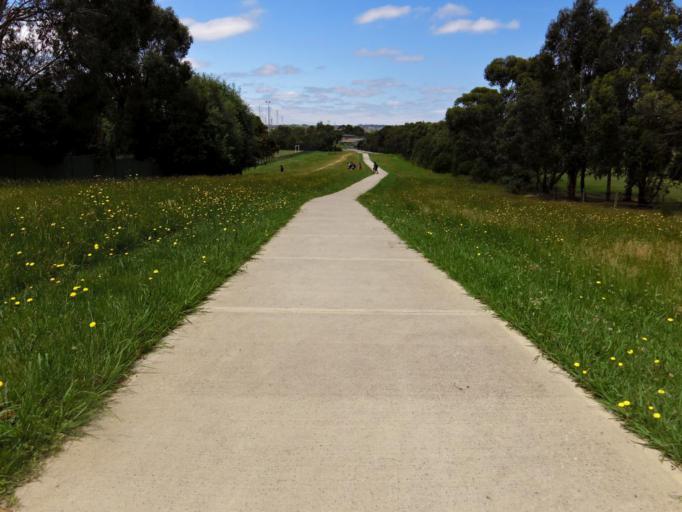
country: AU
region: Victoria
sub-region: Casey
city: Endeavour Hills
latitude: -37.9717
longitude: 145.2741
